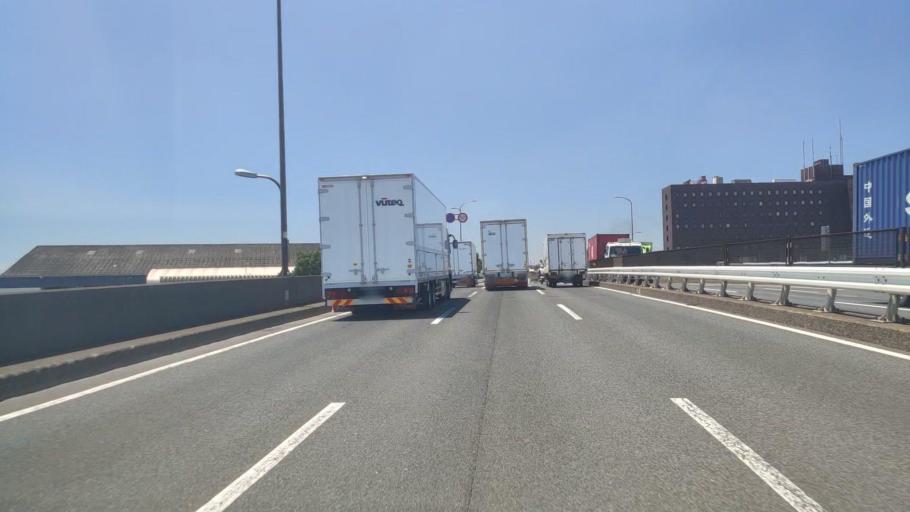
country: JP
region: Aichi
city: Kanie
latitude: 35.0846
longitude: 136.8286
